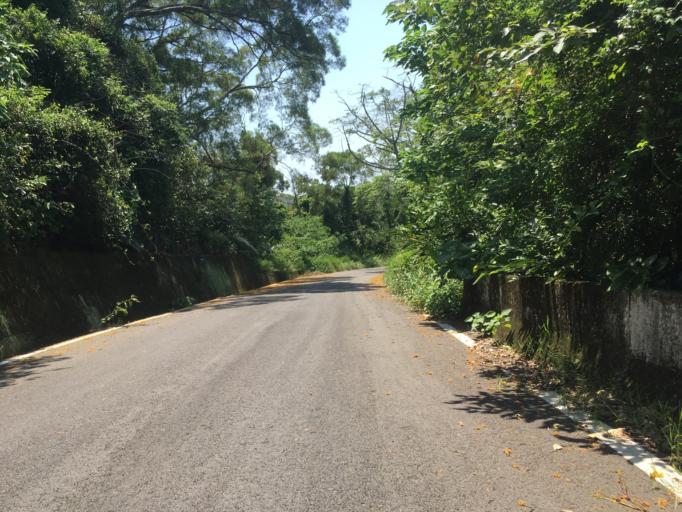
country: TW
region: Taiwan
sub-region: Hsinchu
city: Hsinchu
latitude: 24.7328
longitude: 120.9871
